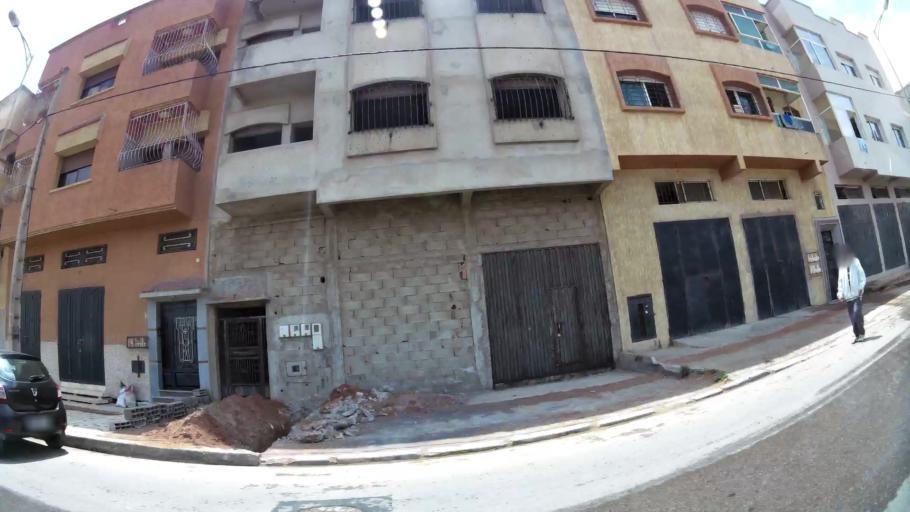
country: MA
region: Rabat-Sale-Zemmour-Zaer
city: Sale
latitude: 34.0631
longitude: -6.8078
